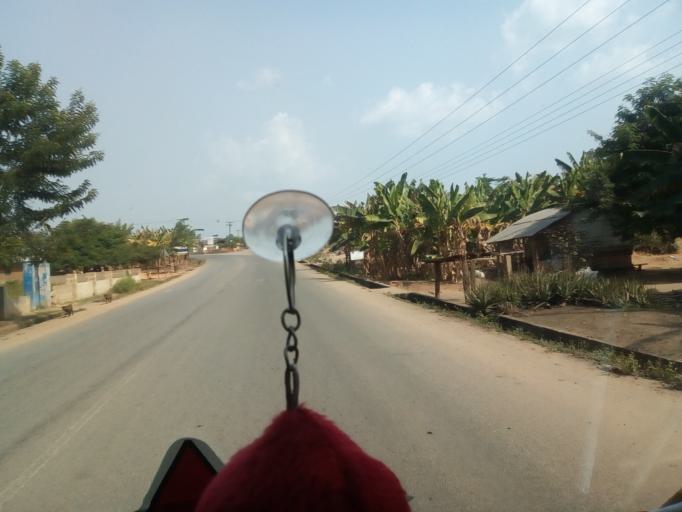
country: GH
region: Eastern
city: Suhum
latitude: 6.0450
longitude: -0.4144
